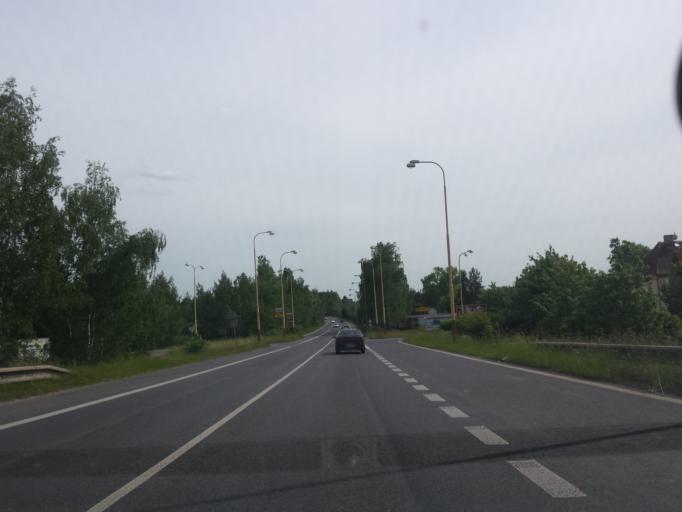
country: CZ
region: Liberecky
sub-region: Okres Ceska Lipa
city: Ceska Lipa
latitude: 50.6764
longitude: 14.5417
